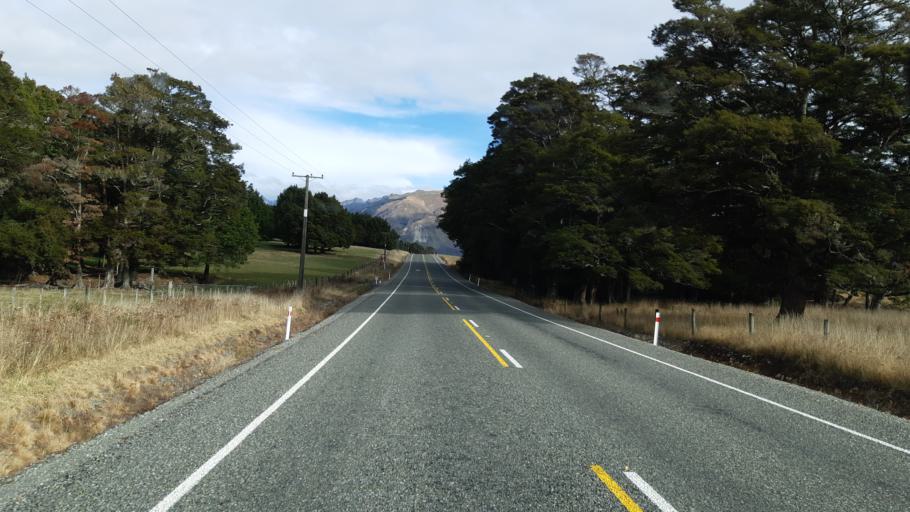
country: NZ
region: Tasman
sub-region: Tasman District
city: Wakefield
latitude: -41.7899
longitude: 172.8829
